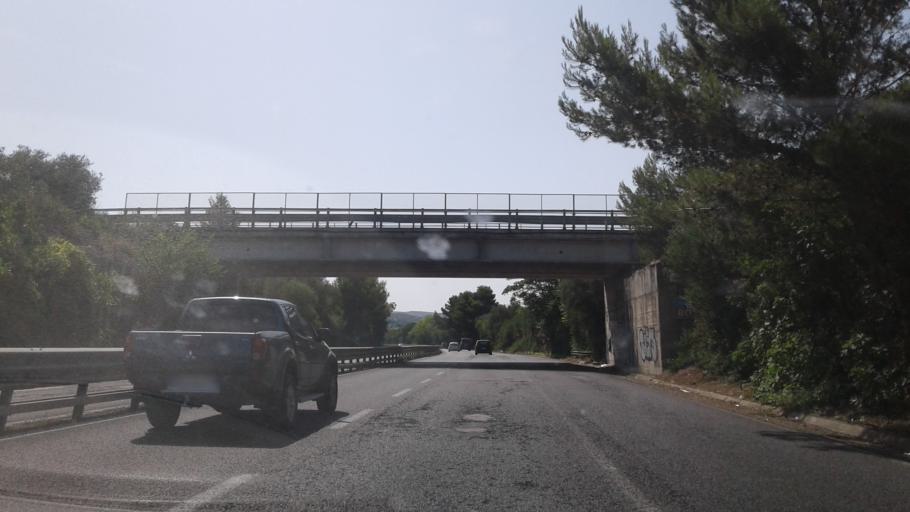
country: IT
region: Sardinia
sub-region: Provincia di Sassari
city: Sassari
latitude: 40.7048
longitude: 8.5518
